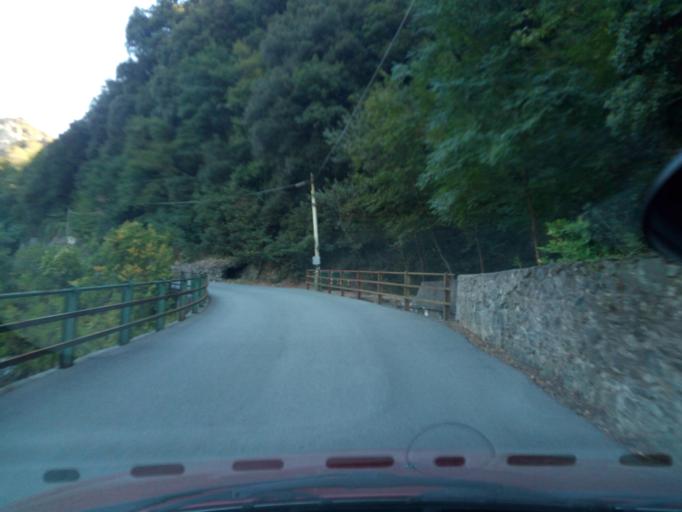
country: IT
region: Liguria
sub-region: Provincia di Genova
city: Mele
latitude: 44.4614
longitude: 8.8216
